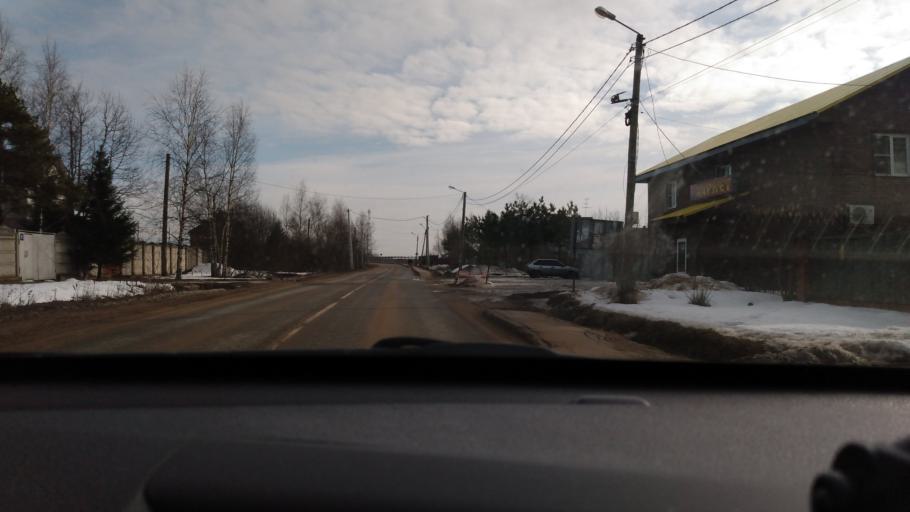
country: RU
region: Moskovskaya
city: Dedovsk
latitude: 55.8933
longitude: 37.1586
